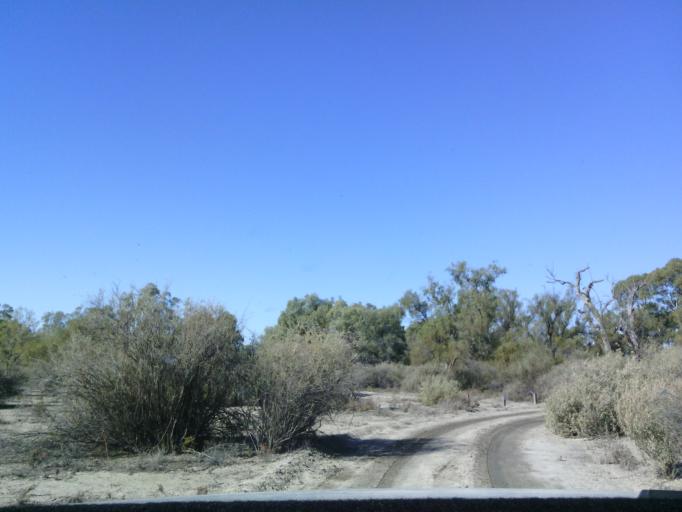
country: AU
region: South Australia
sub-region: Berri and Barmera
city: Berri
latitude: -34.2598
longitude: 140.6903
